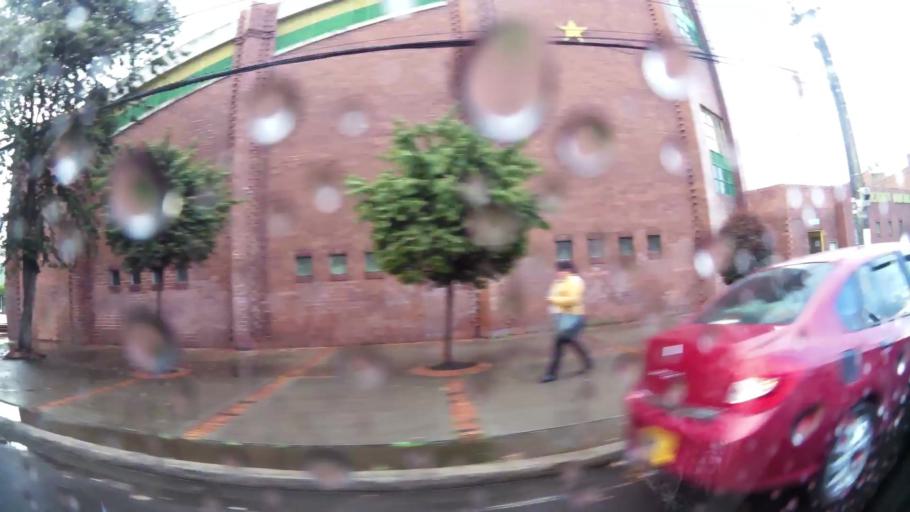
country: CO
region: Cundinamarca
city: Chia
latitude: 4.8628
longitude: -74.0552
